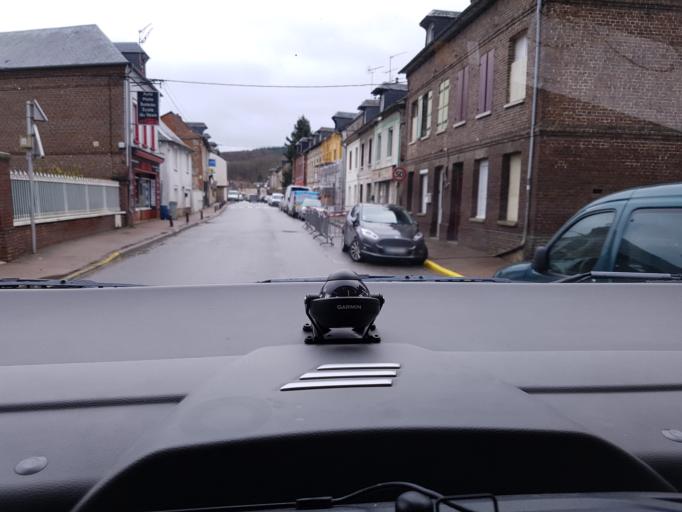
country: FR
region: Haute-Normandie
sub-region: Departement de l'Eure
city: Pont-Saint-Pierre
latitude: 49.3335
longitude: 1.2756
